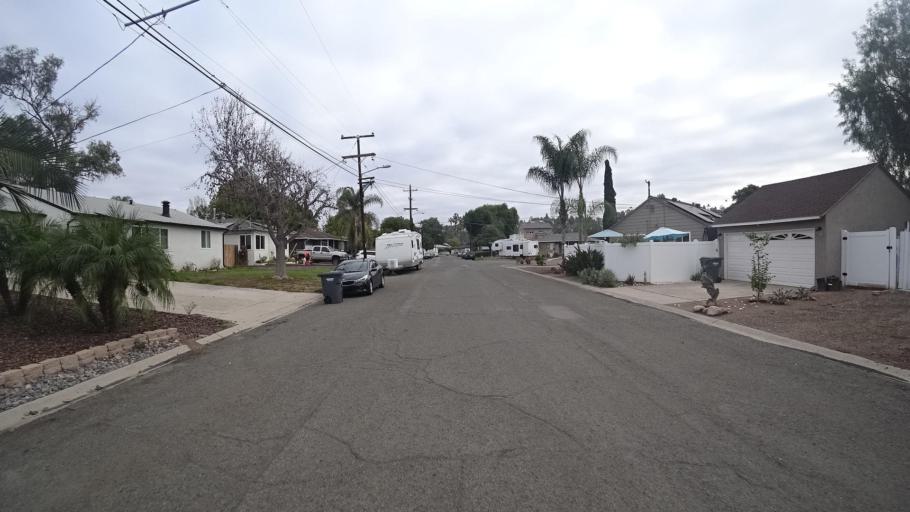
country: US
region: California
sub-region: San Diego County
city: Lemon Grove
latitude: 32.7456
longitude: -117.0167
